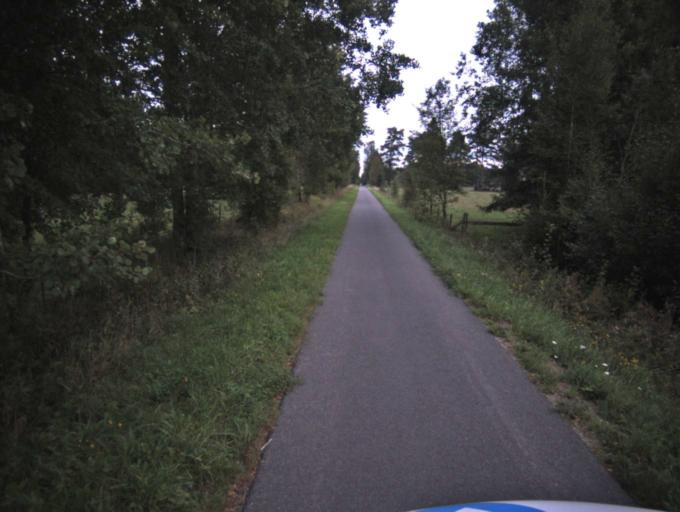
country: SE
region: Vaestra Goetaland
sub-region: Falkopings Kommun
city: Falkoeping
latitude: 58.0049
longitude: 13.5504
